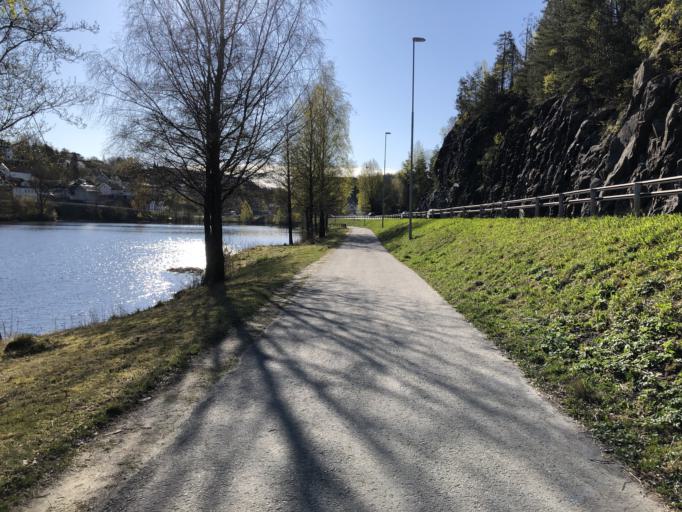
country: NO
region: Aust-Agder
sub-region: Arendal
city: Arendal
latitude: 58.4728
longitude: 8.7536
